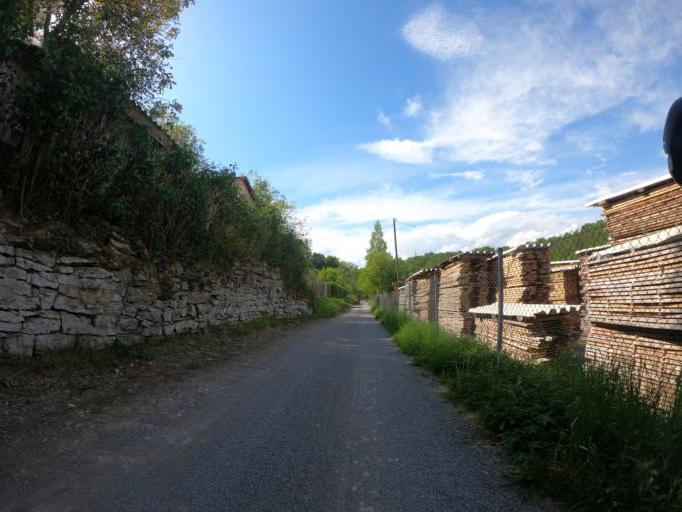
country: DE
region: Baden-Wuerttemberg
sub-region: Regierungsbezirk Stuttgart
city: Ehningen
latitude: 48.6594
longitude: 8.9278
